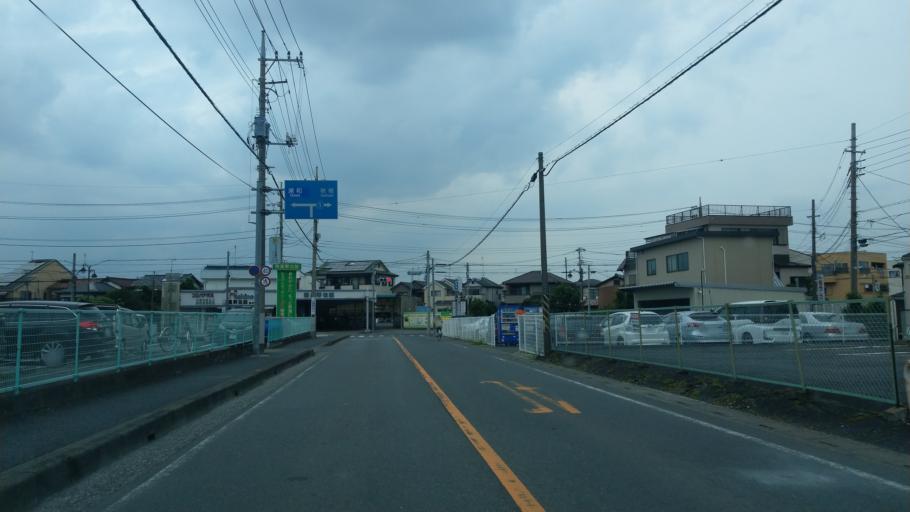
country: JP
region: Saitama
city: Saitama
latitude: 35.8799
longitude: 139.6758
